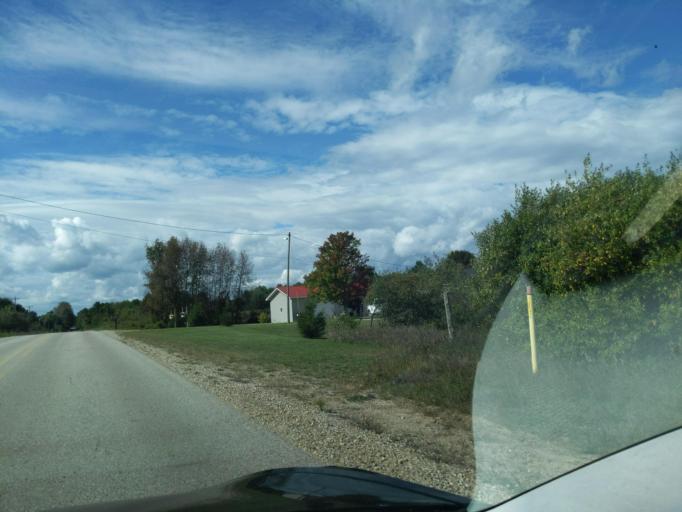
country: US
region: Michigan
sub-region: Antrim County
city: Bellaire
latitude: 45.0347
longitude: -85.3456
